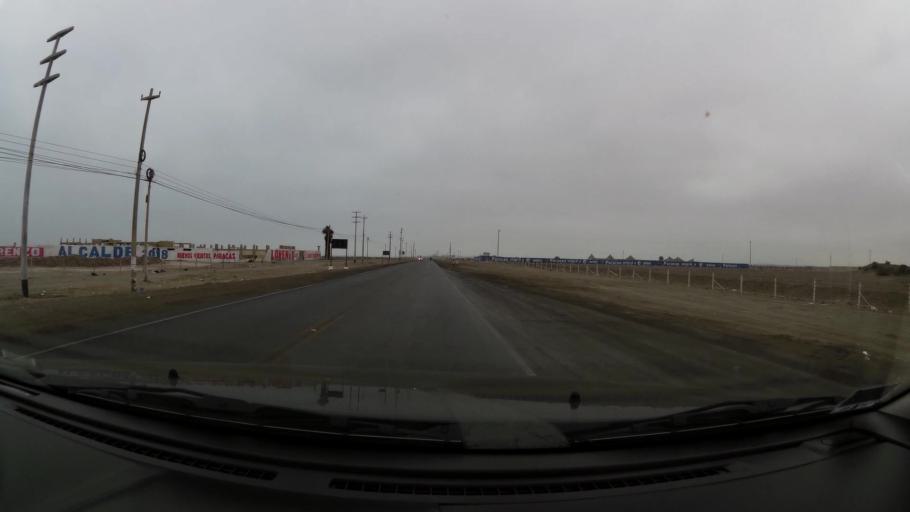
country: PE
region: Ica
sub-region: Provincia de Pisco
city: Pisco
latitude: -13.7661
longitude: -76.2342
